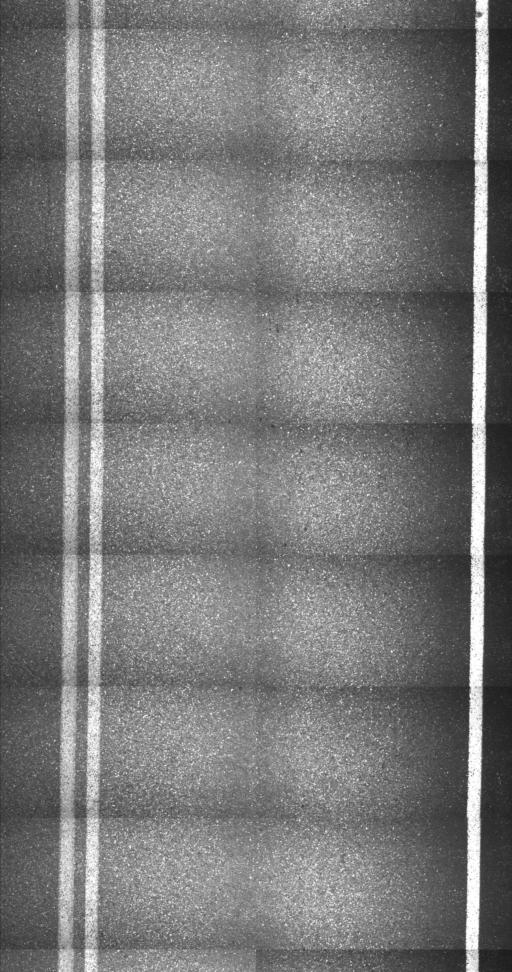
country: US
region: Vermont
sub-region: Orleans County
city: Newport
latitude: 44.9062
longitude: -71.9777
